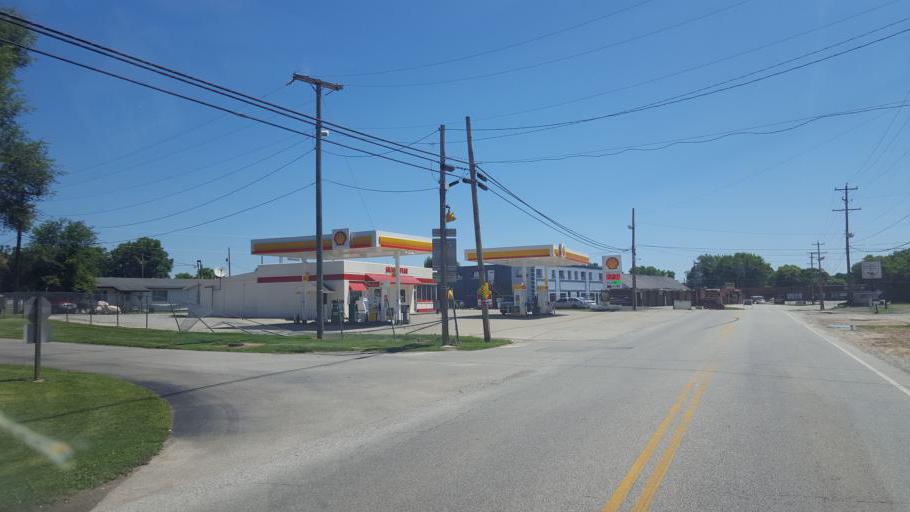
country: US
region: West Virginia
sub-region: Cabell County
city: Pea Ridge
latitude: 38.4425
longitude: -82.3576
